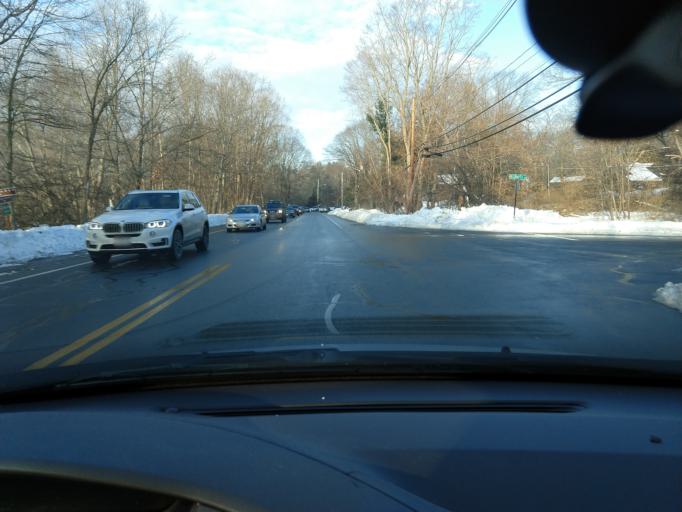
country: US
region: Massachusetts
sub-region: Middlesex County
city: Concord
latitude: 42.4670
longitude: -71.3568
